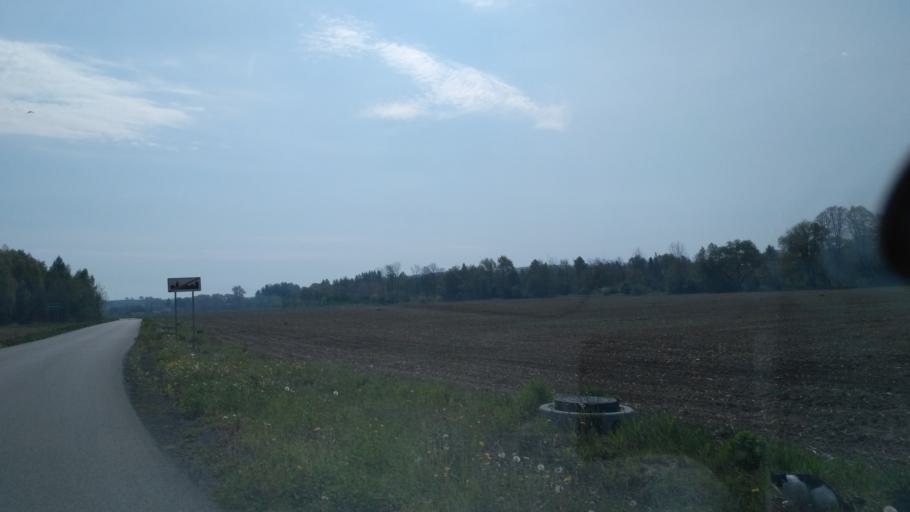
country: PL
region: Subcarpathian Voivodeship
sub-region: Powiat jaroslawski
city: Pruchnik
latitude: 49.9062
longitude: 22.5320
